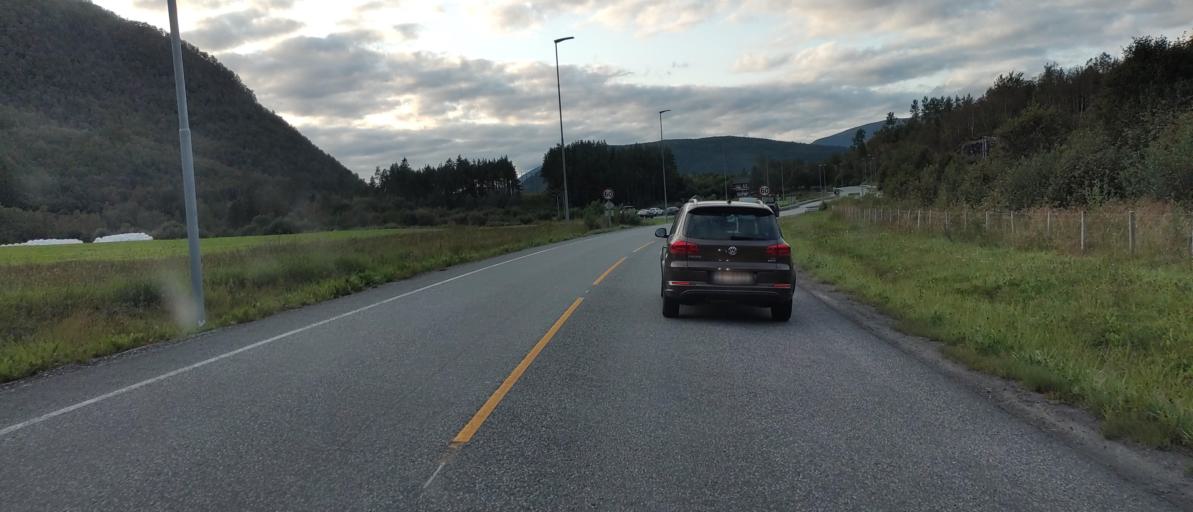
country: NO
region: More og Romsdal
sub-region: Molde
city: Molde
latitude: 62.7905
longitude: 7.2333
